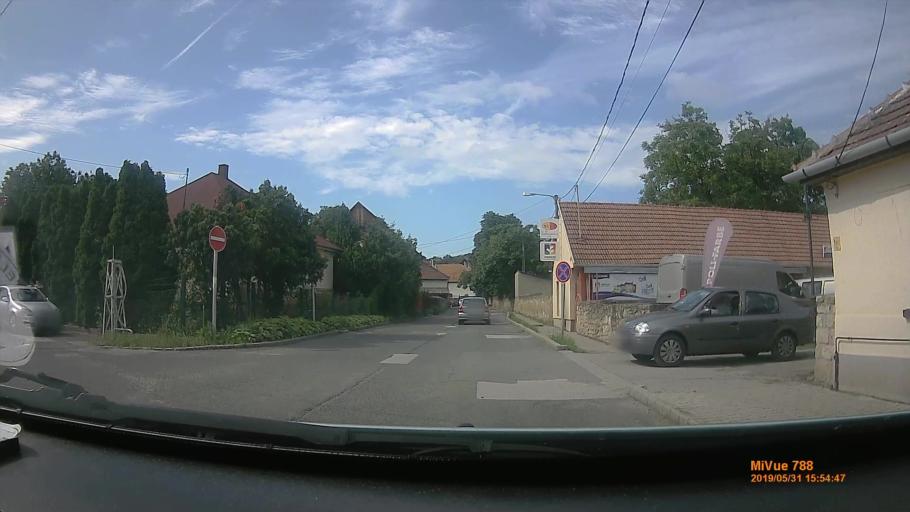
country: HU
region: Borsod-Abauj-Zemplen
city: Szerencs
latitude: 48.1616
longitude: 21.2000
